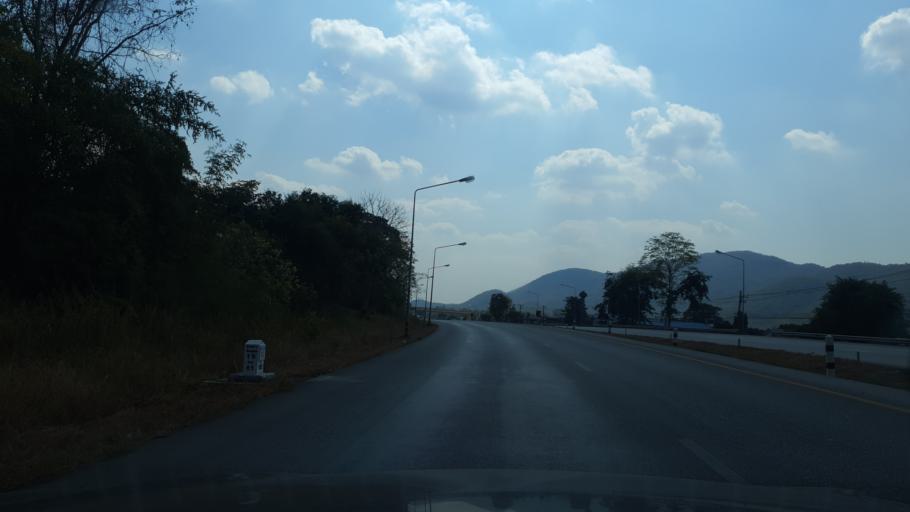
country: TH
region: Lampang
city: Mae Phrik
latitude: 17.3636
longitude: 99.1468
